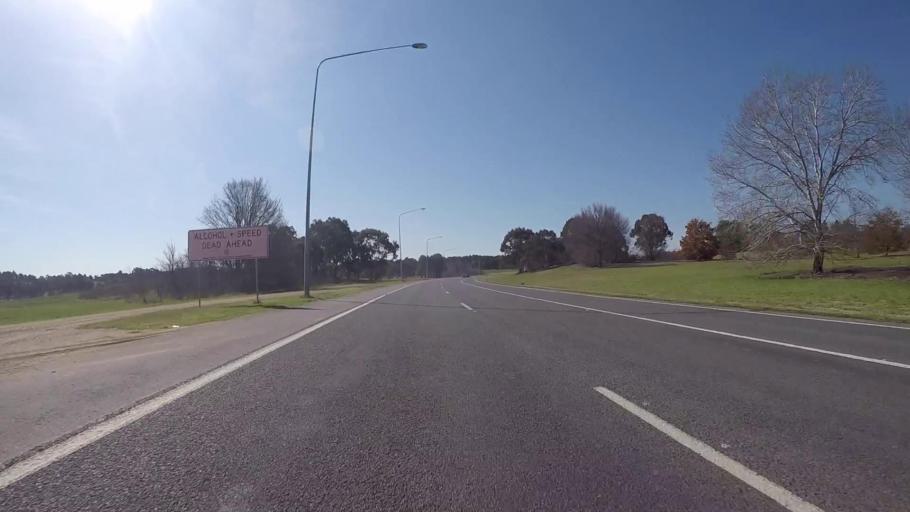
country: AU
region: Australian Capital Territory
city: Forrest
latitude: -35.3189
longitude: 149.0891
